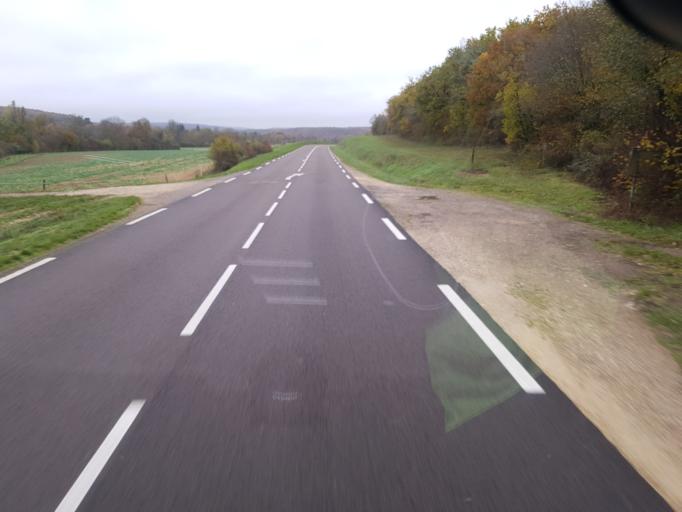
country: FR
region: Bourgogne
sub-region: Departement de la Cote-d'Or
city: Is-sur-Tille
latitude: 47.5266
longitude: 4.9974
